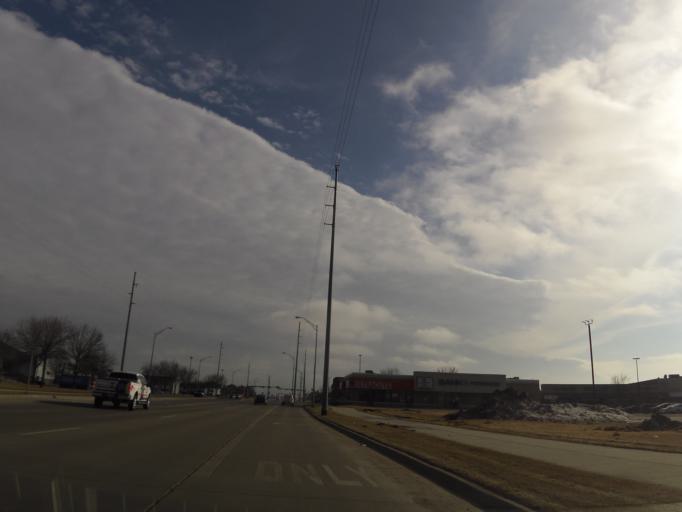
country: US
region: North Dakota
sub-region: Grand Forks County
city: Grand Forks
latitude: 47.8887
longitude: -97.0668
